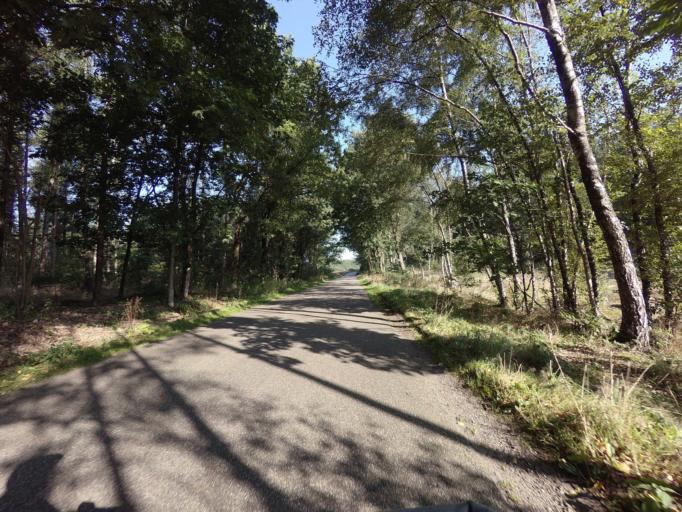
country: DE
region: Lower Saxony
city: Wielen
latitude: 52.5330
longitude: 6.7271
